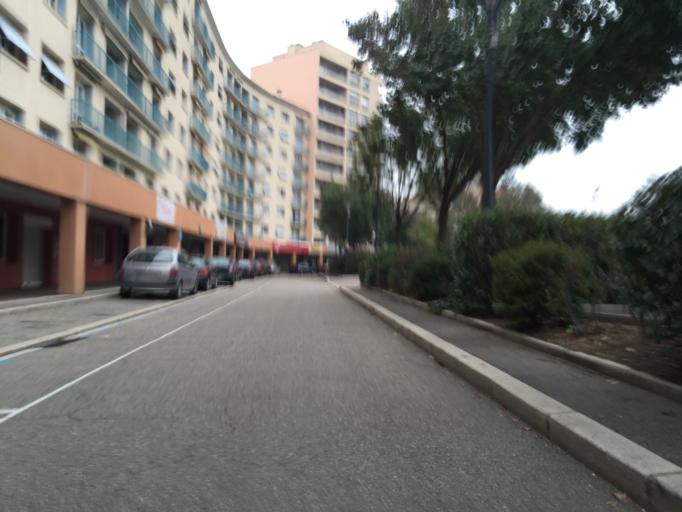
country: FR
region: Rhone-Alpes
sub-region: Departement de la Loire
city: Saint-Chamond
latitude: 45.4756
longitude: 4.5073
